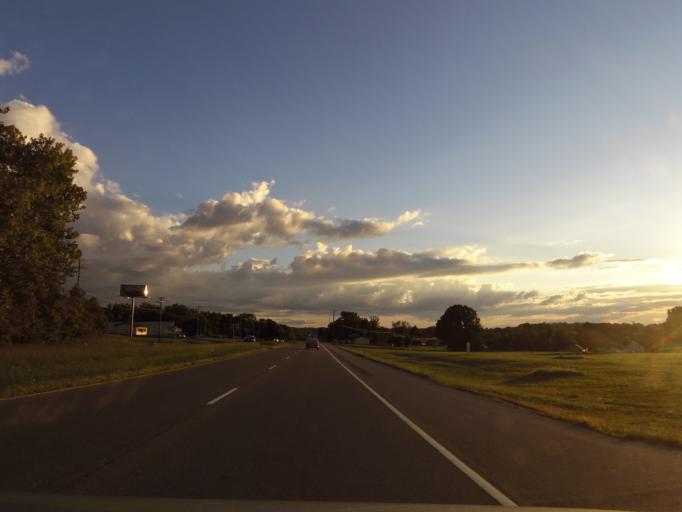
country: US
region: Tennessee
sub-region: Knox County
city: Mascot
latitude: 36.0404
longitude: -83.7186
